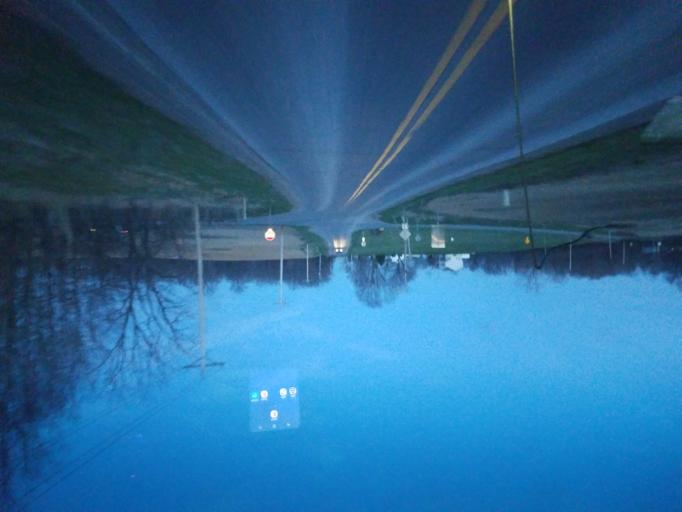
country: US
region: Ohio
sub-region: Logan County
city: De Graff
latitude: 40.3510
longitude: -83.9327
